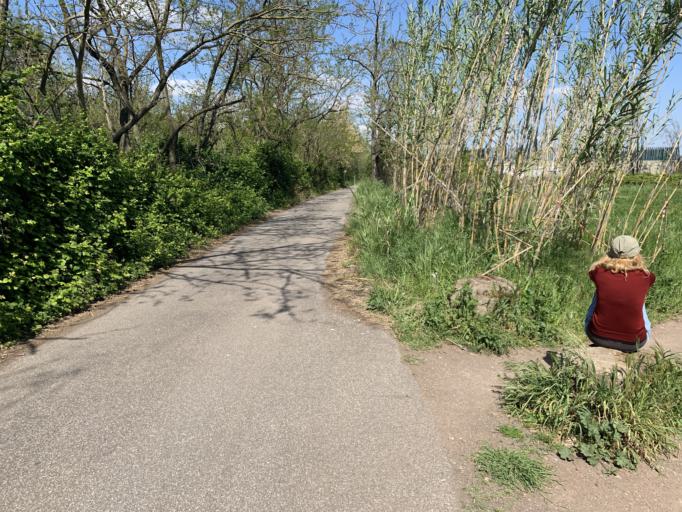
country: IT
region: Latium
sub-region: Citta metropolitana di Roma Capitale
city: Ciampino
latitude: 41.8352
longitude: 12.5692
